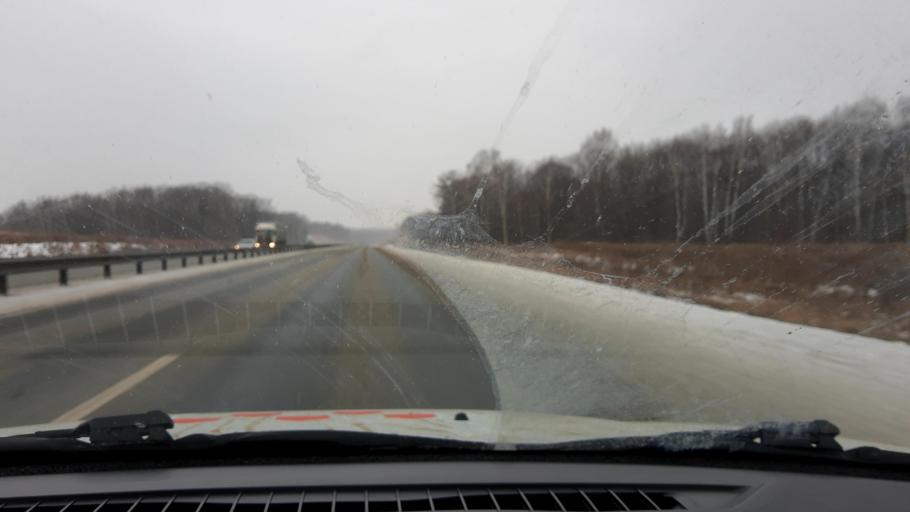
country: RU
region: Nizjnij Novgorod
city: Kstovo
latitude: 56.1007
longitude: 44.0433
